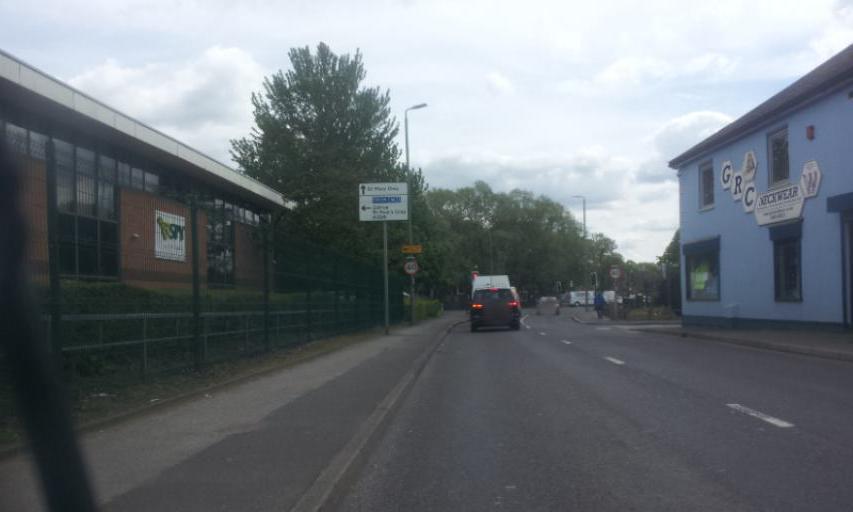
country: GB
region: England
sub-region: Greater London
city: Orpington
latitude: 51.3884
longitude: 0.1084
